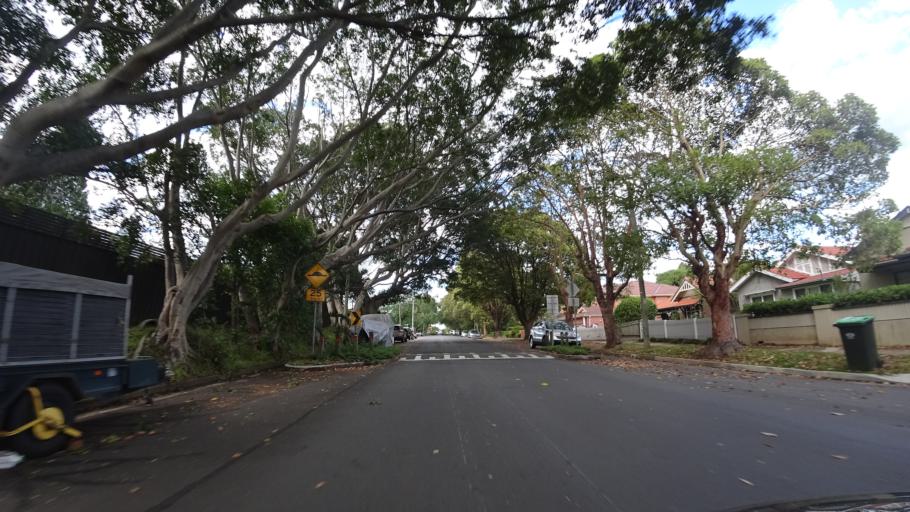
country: AU
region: New South Wales
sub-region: Willoughby
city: Chatswood
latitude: -33.7981
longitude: 151.1924
